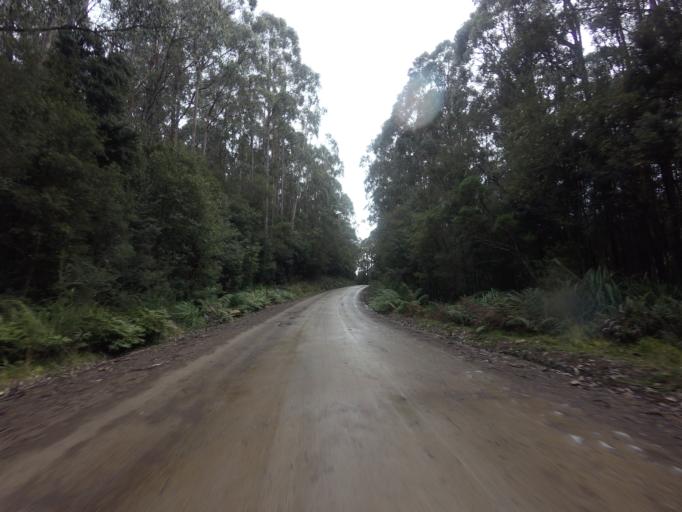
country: AU
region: Tasmania
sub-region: Huon Valley
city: Geeveston
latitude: -43.4843
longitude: 146.8915
